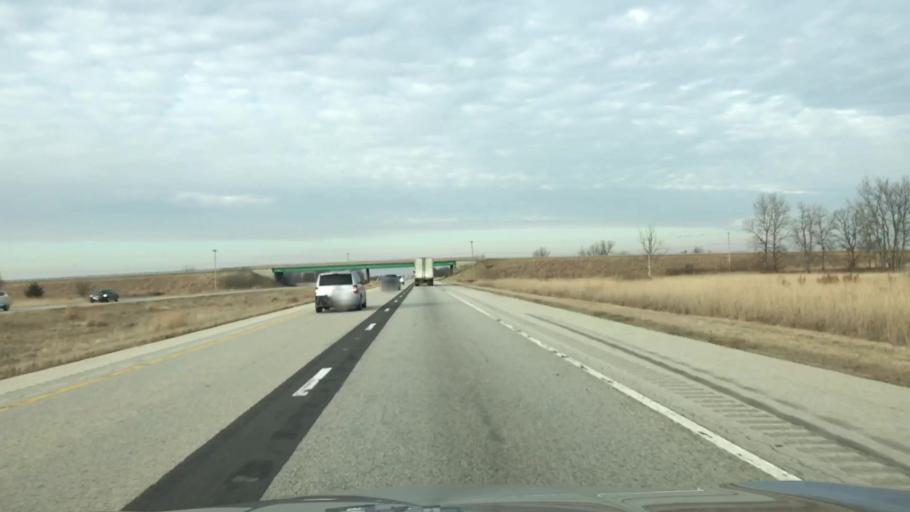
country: US
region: Illinois
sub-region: Sangamon County
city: Divernon
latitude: 39.5652
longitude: -89.6460
